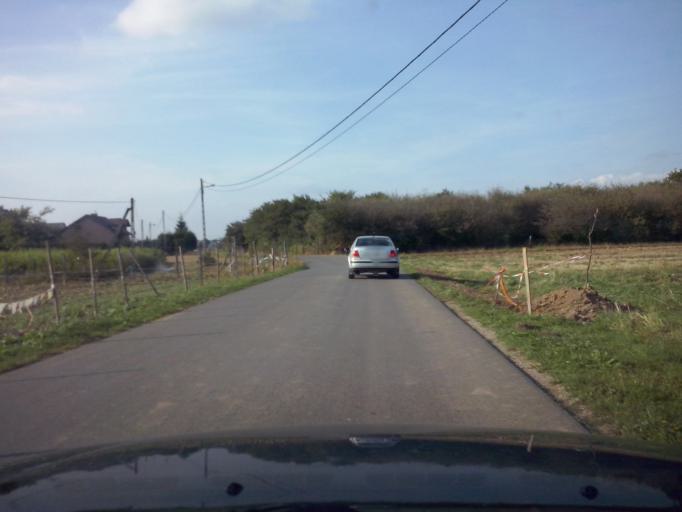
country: PL
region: Subcarpathian Voivodeship
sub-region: Powiat nizanski
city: Krzeszow
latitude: 50.3951
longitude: 22.3216
